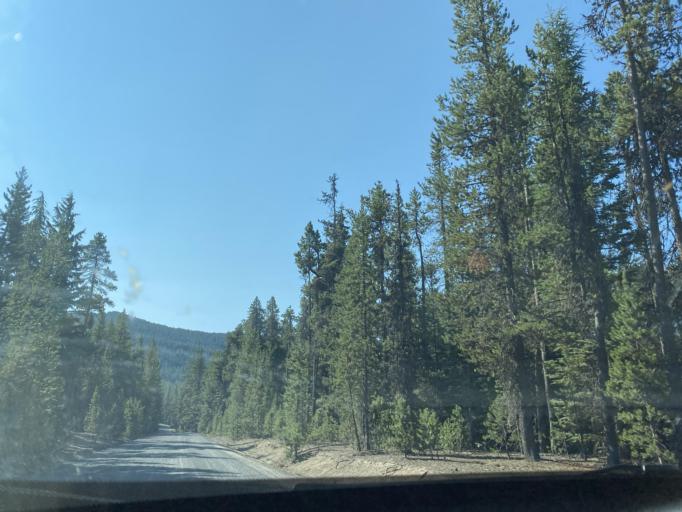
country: US
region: Oregon
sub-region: Deschutes County
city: Three Rivers
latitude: 43.7039
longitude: -121.2745
